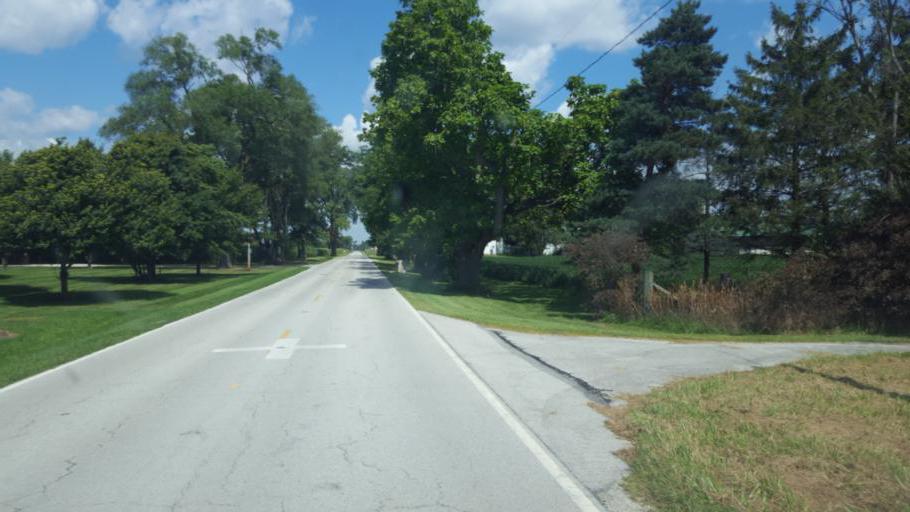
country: US
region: Ohio
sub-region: Sandusky County
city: Gibsonburg
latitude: 41.2908
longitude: -83.3108
